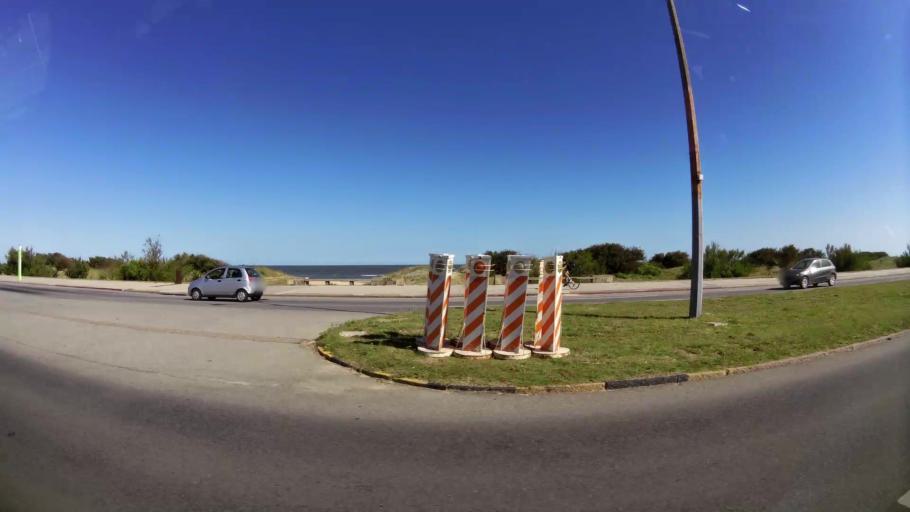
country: UY
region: Canelones
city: Barra de Carrasco
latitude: -34.8848
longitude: -56.0412
